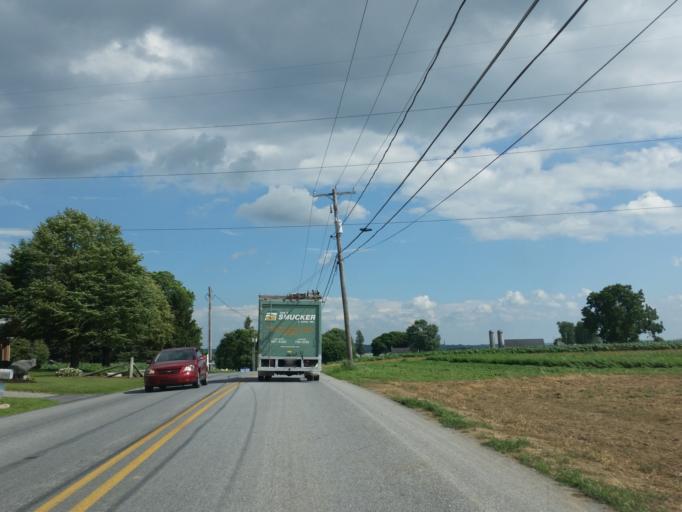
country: US
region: Pennsylvania
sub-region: Lancaster County
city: Lampeter
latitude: 40.0077
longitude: -76.2210
